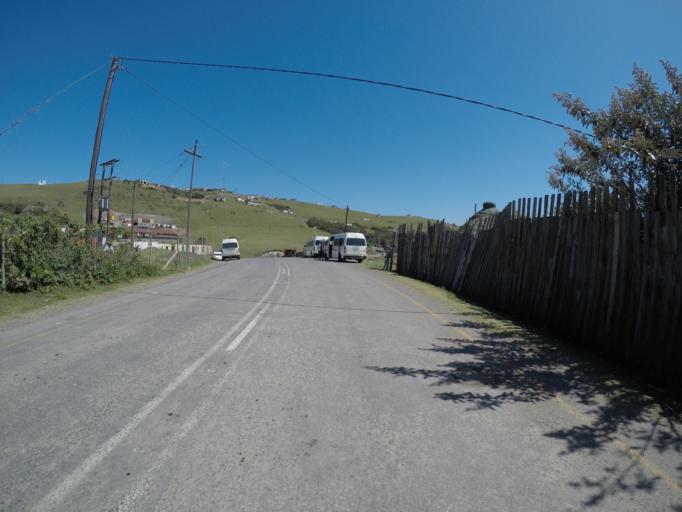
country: ZA
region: Eastern Cape
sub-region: OR Tambo District Municipality
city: Libode
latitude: -31.9841
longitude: 29.1484
